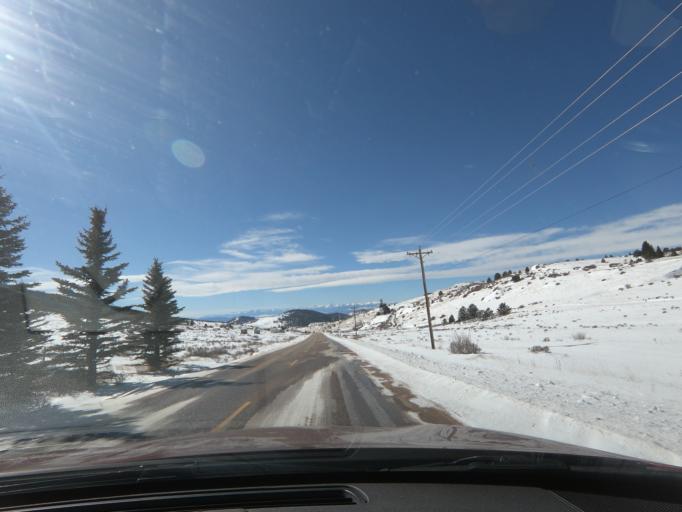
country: US
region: Colorado
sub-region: Teller County
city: Cripple Creek
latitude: 38.7266
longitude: -105.1211
